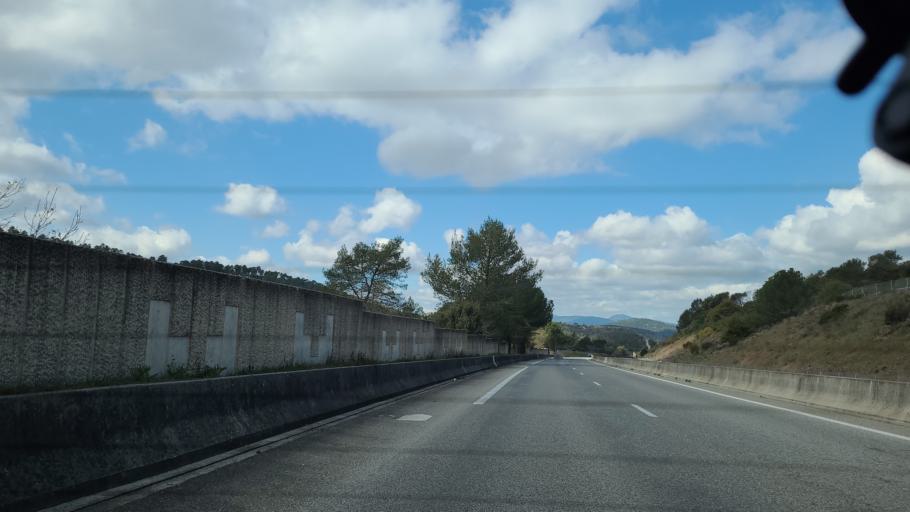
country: FR
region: Provence-Alpes-Cote d'Azur
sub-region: Departement du Var
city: Pignans
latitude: 43.2887
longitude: 6.2445
